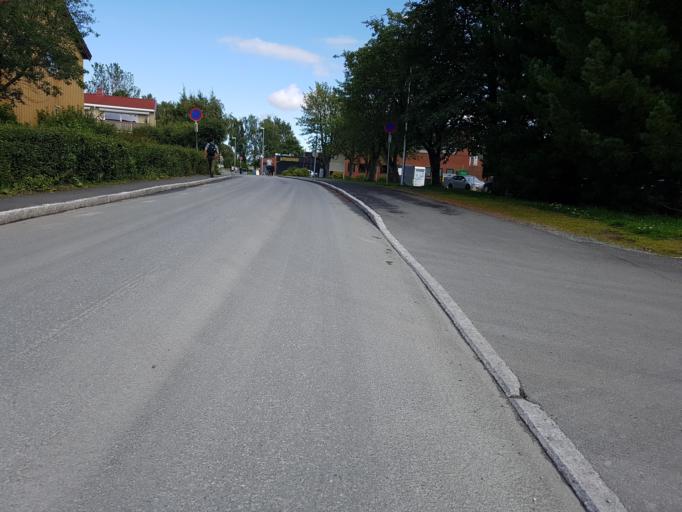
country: NO
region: Sor-Trondelag
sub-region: Trondheim
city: Trondheim
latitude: 63.4127
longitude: 10.4287
